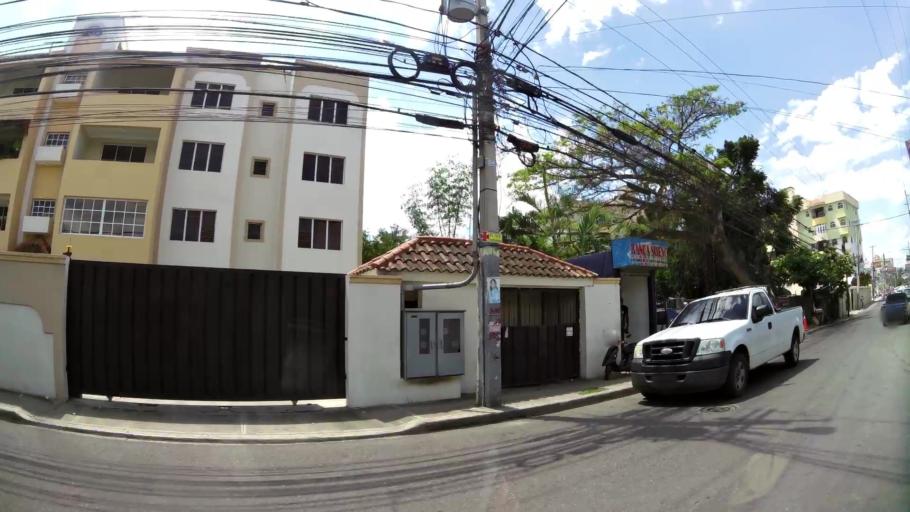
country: DO
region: Santiago
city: Santiago de los Caballeros
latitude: 19.4589
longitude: -70.6670
